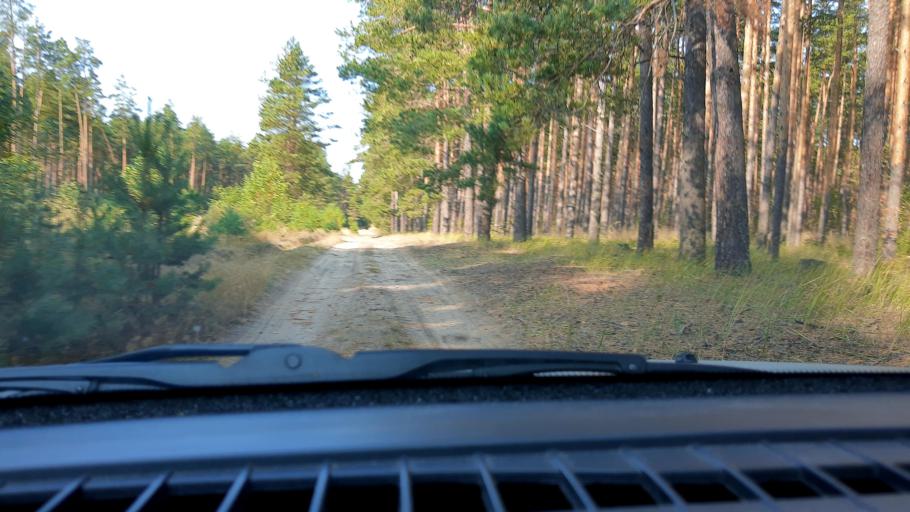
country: RU
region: Nizjnij Novgorod
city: Lukino
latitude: 56.4044
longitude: 43.6398
